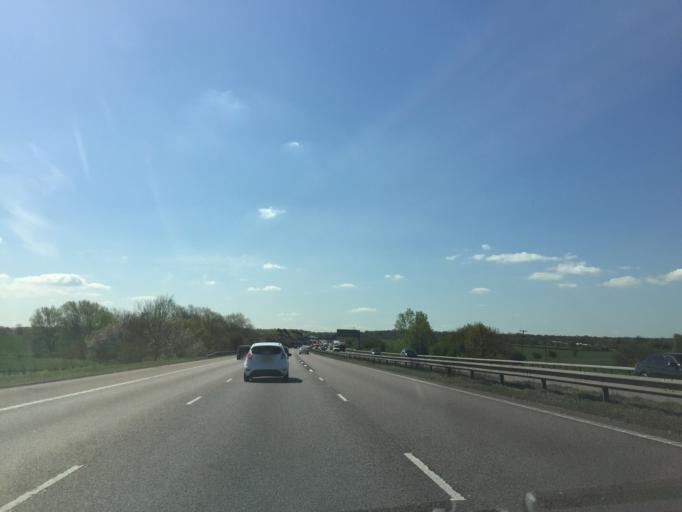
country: GB
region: England
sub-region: Essex
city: Epping
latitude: 51.7300
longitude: 0.1398
